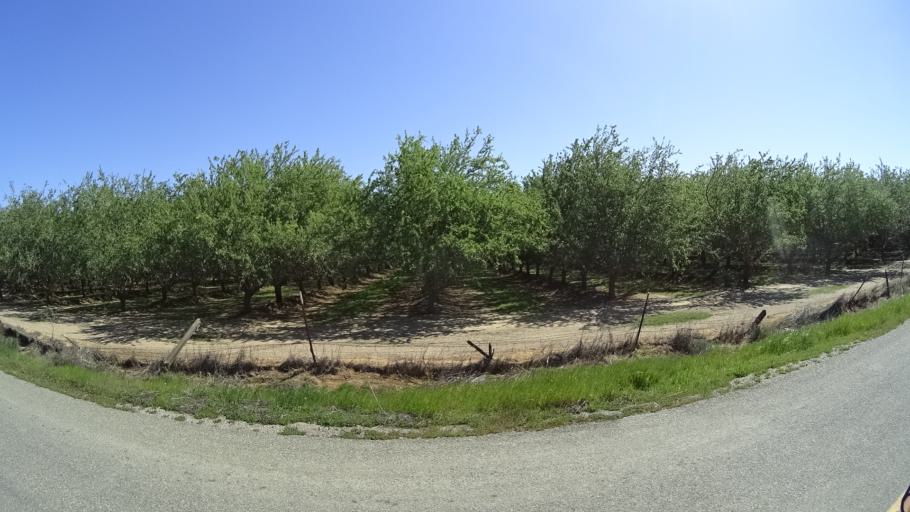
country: US
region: California
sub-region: Glenn County
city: Orland
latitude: 39.6841
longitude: -122.2716
